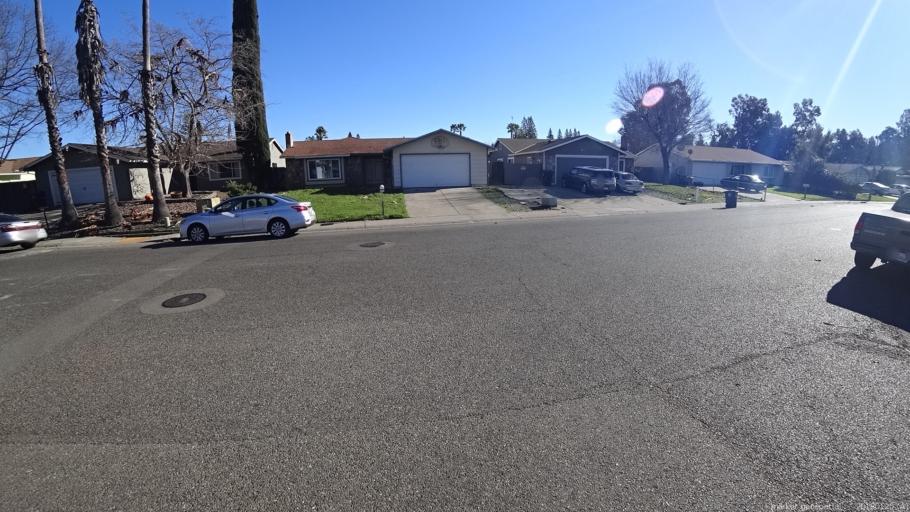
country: US
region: California
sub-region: Sacramento County
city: Rancho Cordova
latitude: 38.5710
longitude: -121.3097
